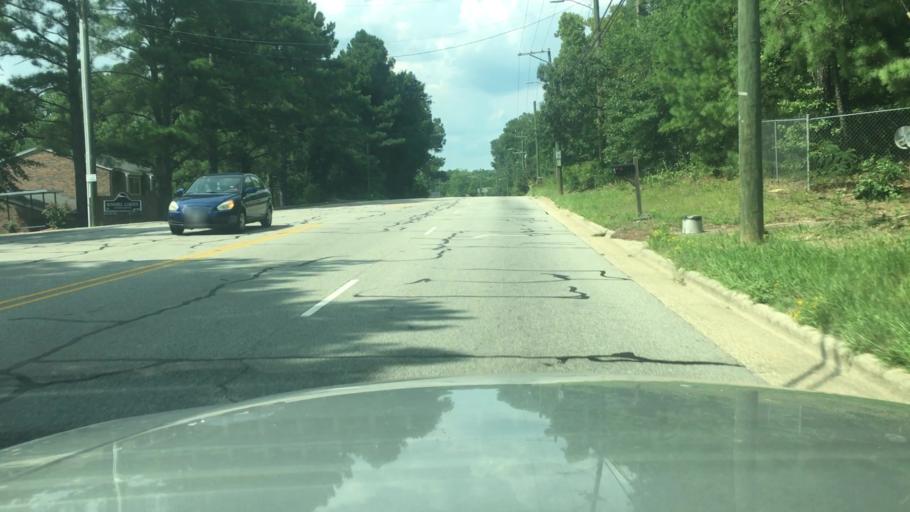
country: US
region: North Carolina
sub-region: Cumberland County
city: Fayetteville
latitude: 35.0846
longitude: -78.8830
